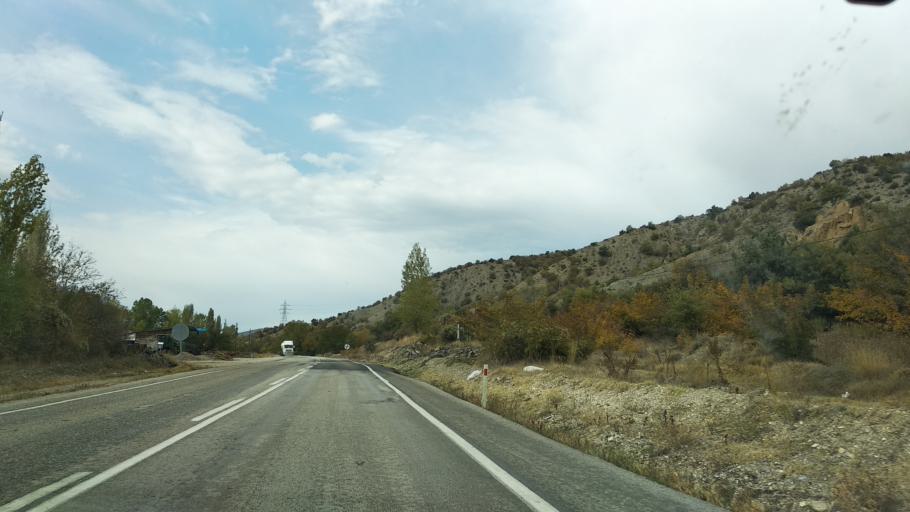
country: TR
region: Ankara
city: Nallihan
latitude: 40.3079
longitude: 31.2876
